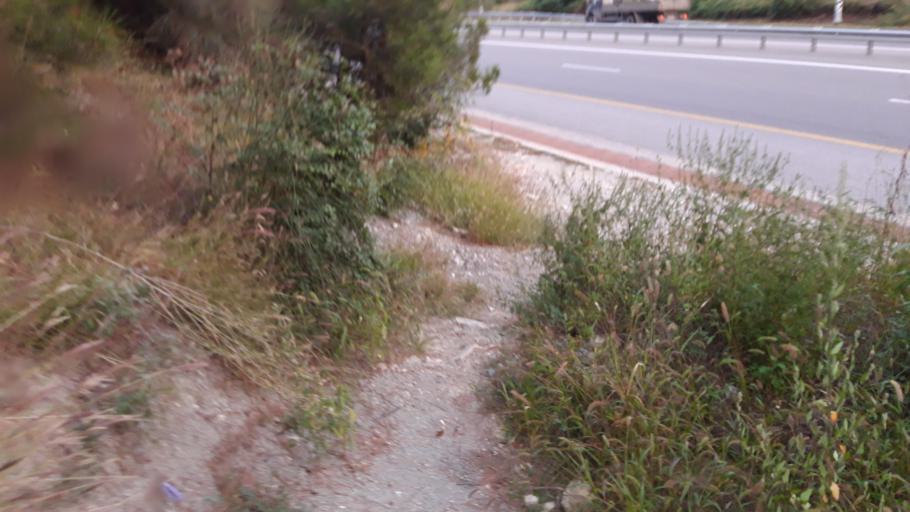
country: RU
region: Krasnodarskiy
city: Gelendzhik
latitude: 44.5793
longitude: 38.0859
